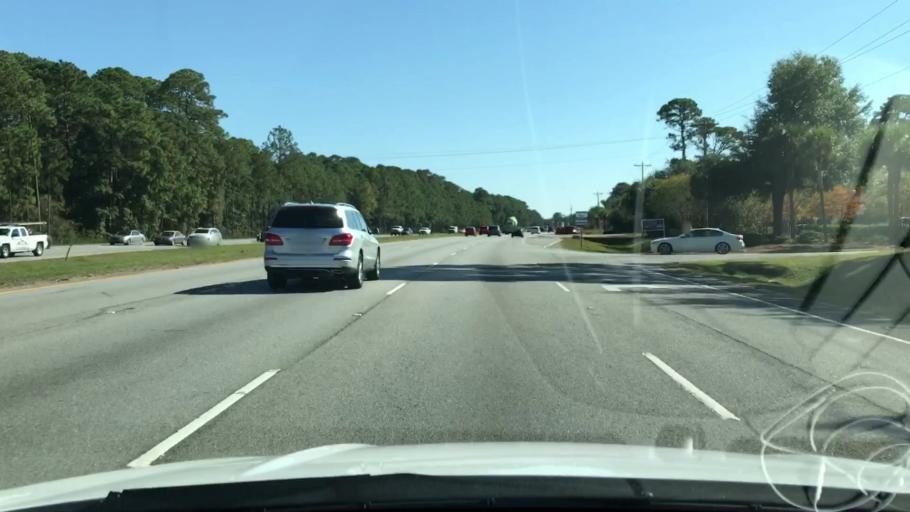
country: US
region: South Carolina
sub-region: Beaufort County
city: Bluffton
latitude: 32.2470
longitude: -80.8311
